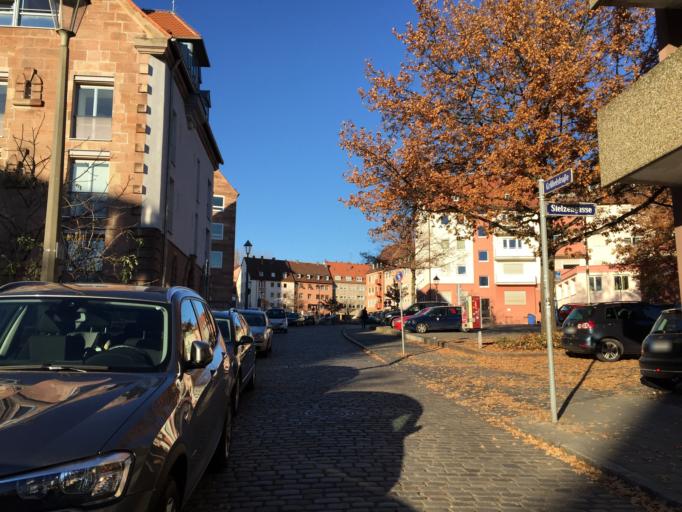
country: DE
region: Bavaria
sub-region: Regierungsbezirk Mittelfranken
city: Nuernberg
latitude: 49.4550
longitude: 11.0840
